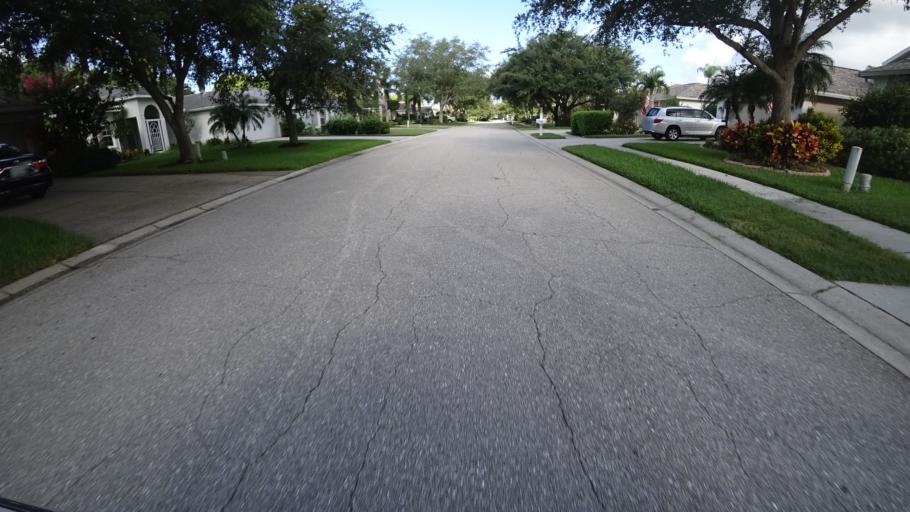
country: US
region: Florida
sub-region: Sarasota County
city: Desoto Lakes
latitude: 27.4221
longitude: -82.4928
